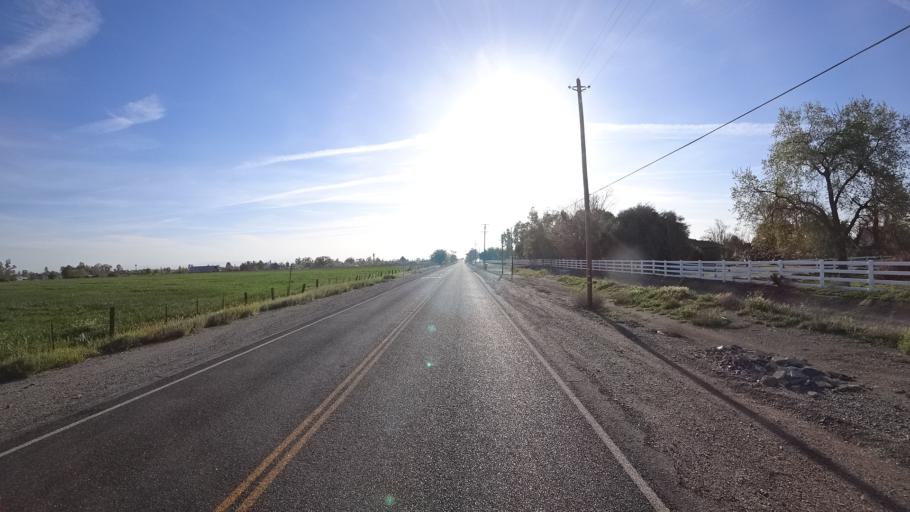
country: US
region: California
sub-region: Glenn County
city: Orland
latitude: 39.7404
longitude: -122.2143
